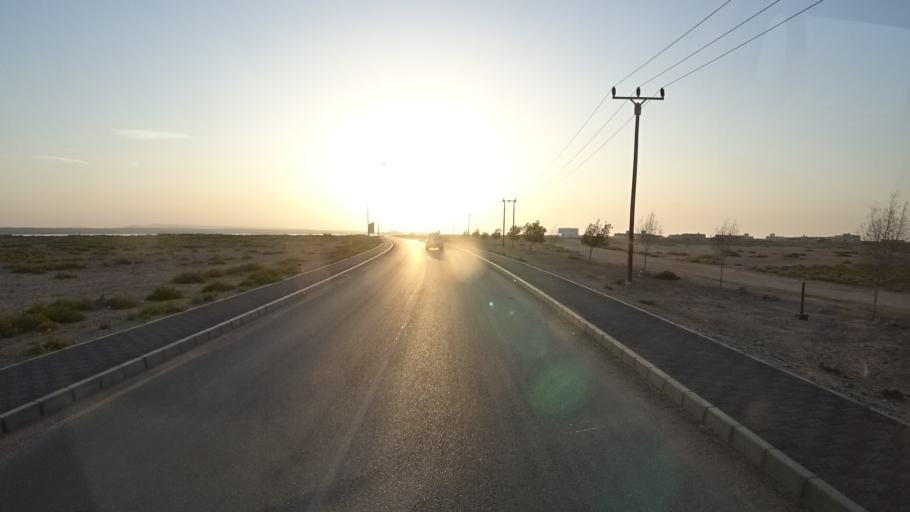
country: OM
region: Ash Sharqiyah
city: Sur
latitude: 22.5267
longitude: 59.7880
